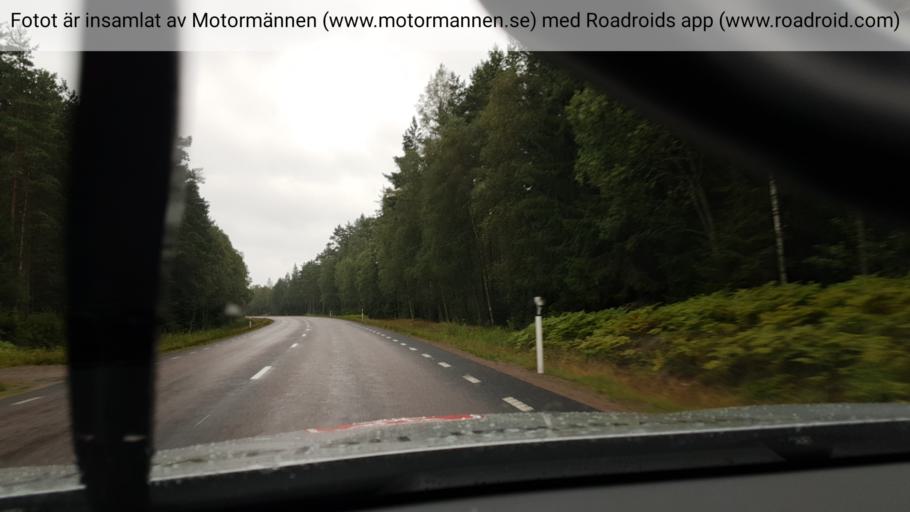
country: SE
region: Vaestra Goetaland
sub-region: Amals Kommun
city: Amal
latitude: 59.0290
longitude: 12.6723
